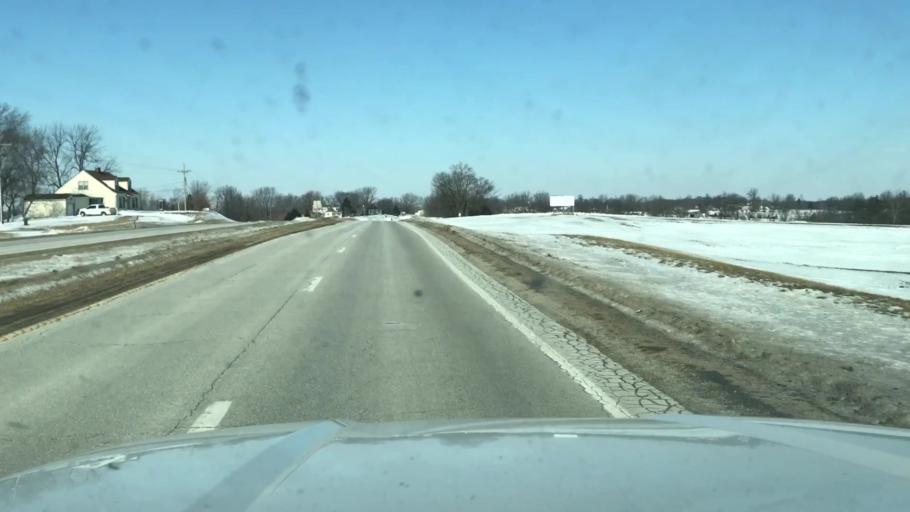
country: US
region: Missouri
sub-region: Andrew County
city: Country Club Village
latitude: 39.8873
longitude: -94.8094
